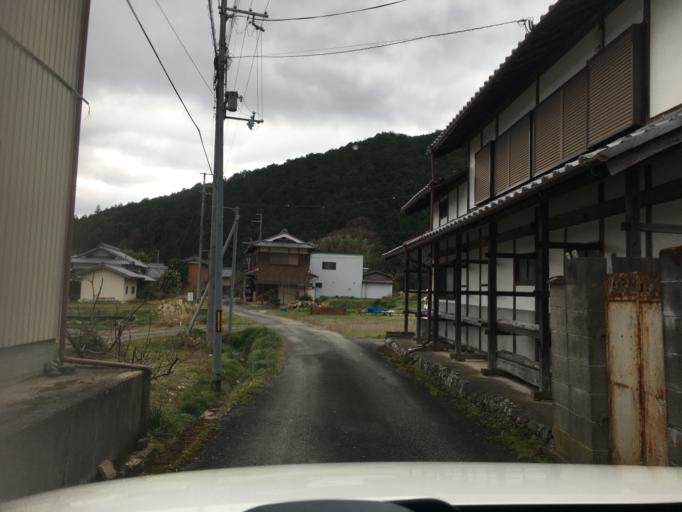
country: JP
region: Kyoto
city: Kameoka
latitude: 35.0393
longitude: 135.4763
